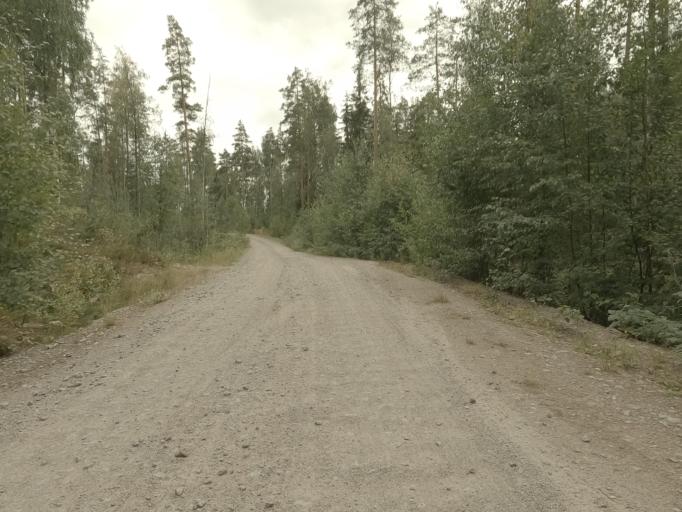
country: RU
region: Leningrad
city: Kamennogorsk
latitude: 60.9797
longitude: 29.1714
